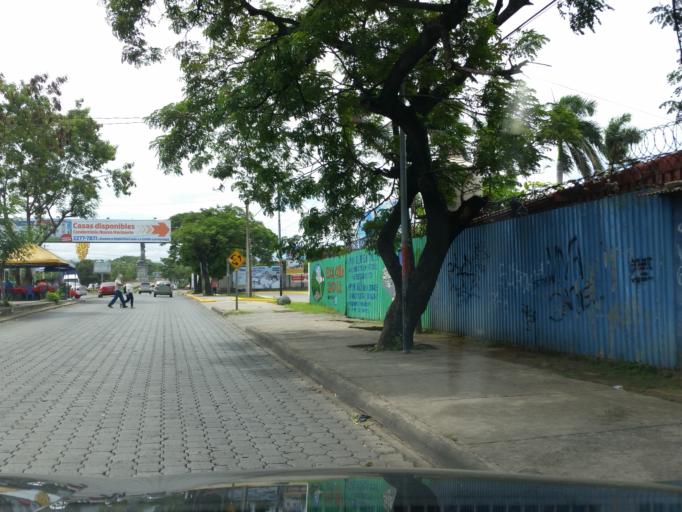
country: NI
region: Managua
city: Managua
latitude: 12.1456
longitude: -86.2243
